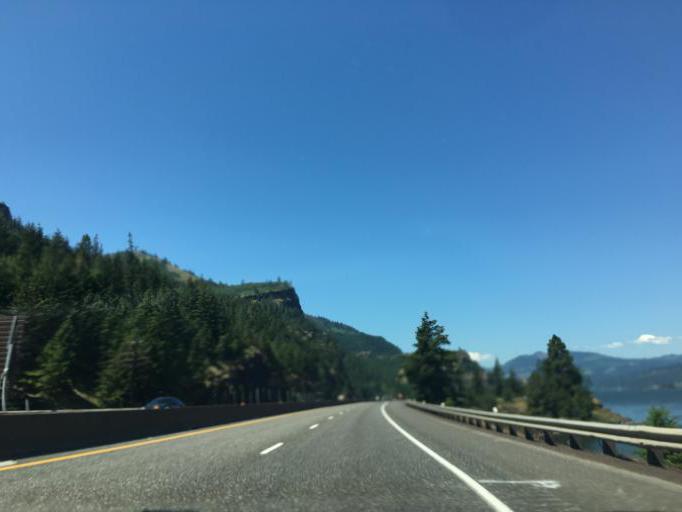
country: US
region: Washington
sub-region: Klickitat County
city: White Salmon
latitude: 45.6864
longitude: -121.4235
